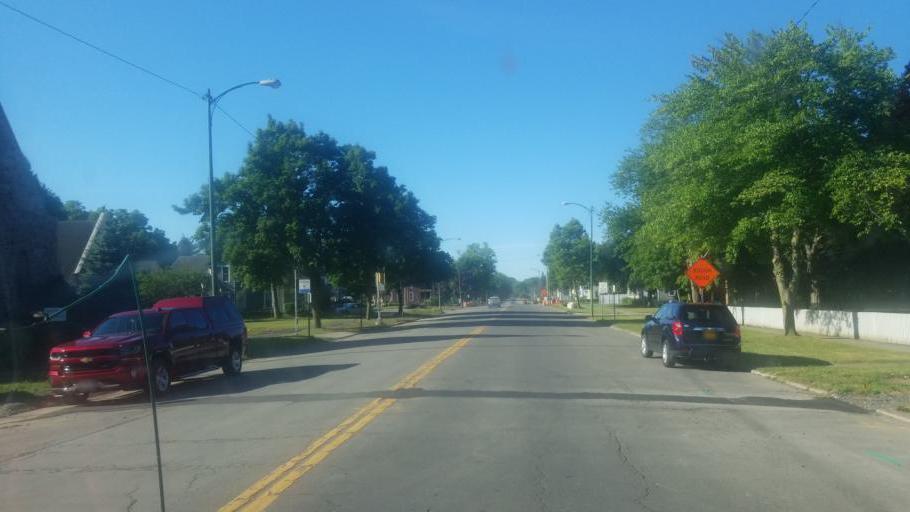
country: US
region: New York
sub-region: Wayne County
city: Newark
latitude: 43.0427
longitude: -77.0956
